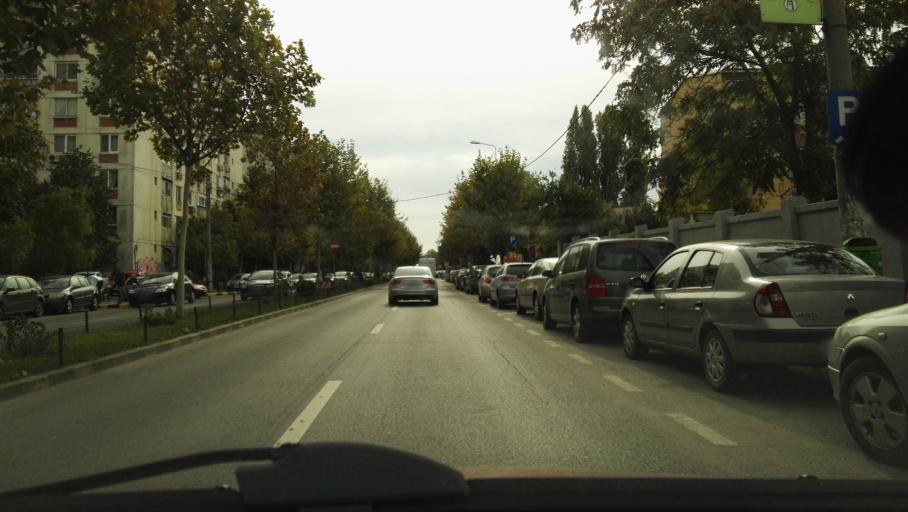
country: RO
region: Ilfov
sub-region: Comuna Popesti-Leordeni
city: Popesti-Leordeni
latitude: 44.3912
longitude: 26.1239
